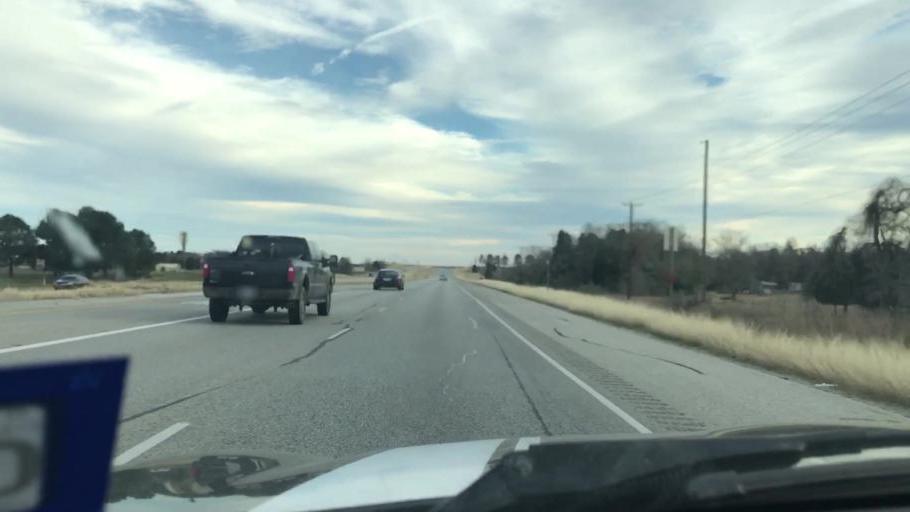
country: US
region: Texas
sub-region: Bastrop County
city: Elgin
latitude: 30.3191
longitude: -97.3158
